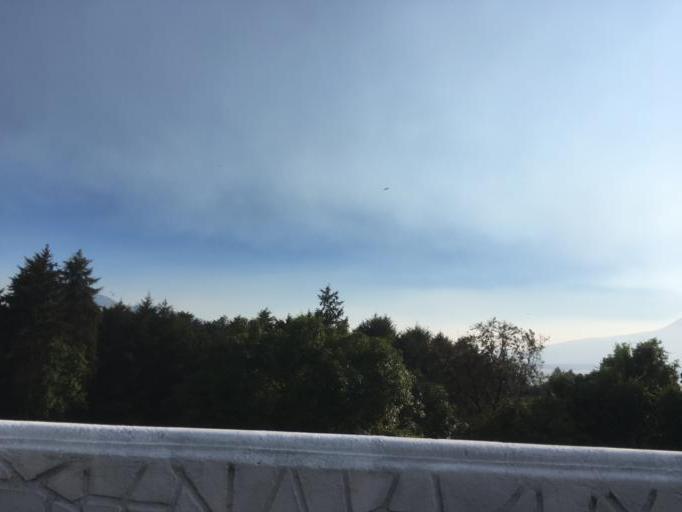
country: MX
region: Michoacan
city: Santa Fe de la Laguna
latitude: 19.6806
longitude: -101.5766
